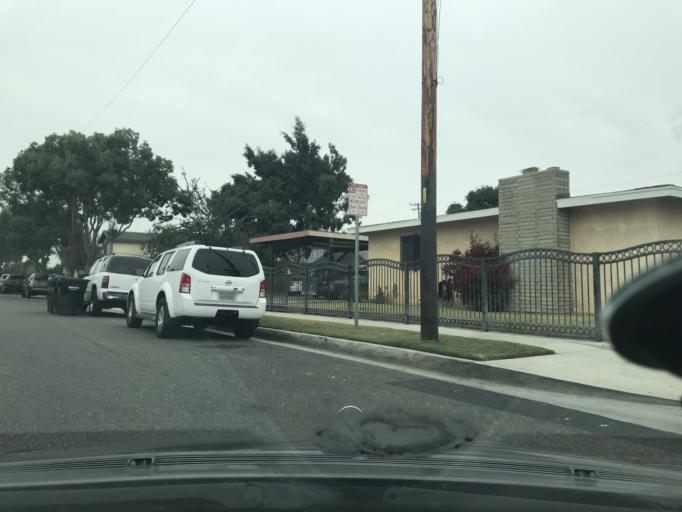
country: US
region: California
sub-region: Los Angeles County
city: Bell Gardens
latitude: 33.9612
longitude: -118.1565
